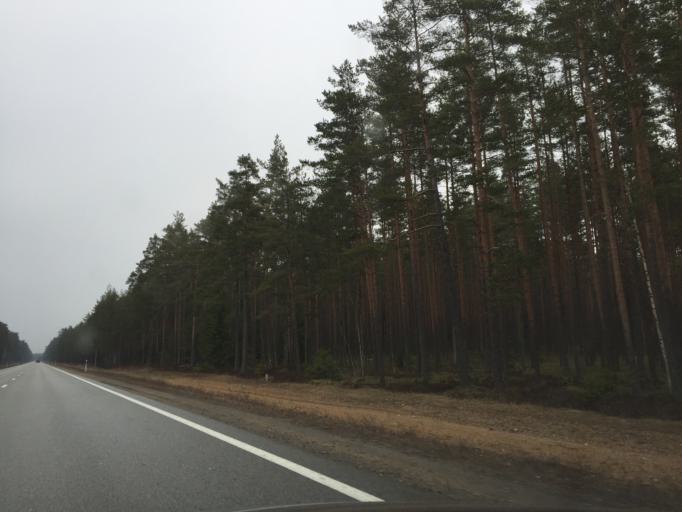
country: LV
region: Salacgrivas
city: Salacgriva
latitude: 57.5522
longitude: 24.4331
